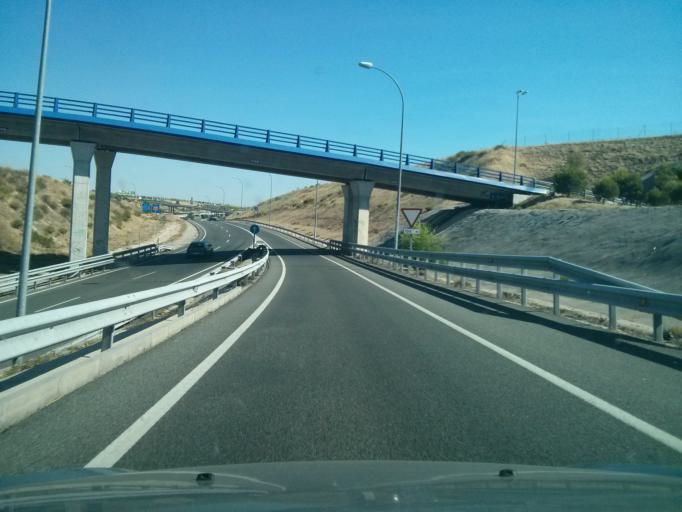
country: ES
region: Madrid
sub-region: Provincia de Madrid
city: Hortaleza
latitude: 40.4963
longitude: -3.6480
